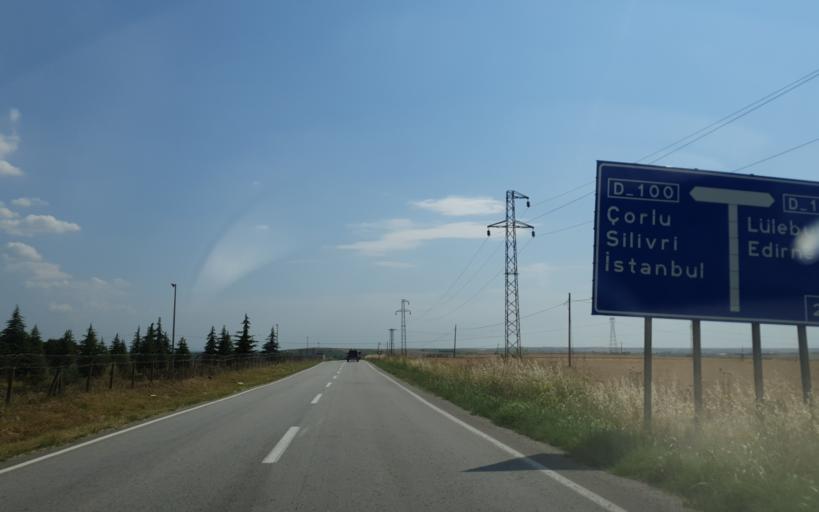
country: TR
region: Kirklareli
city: Buyukkaristiran
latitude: 41.3111
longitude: 27.5162
